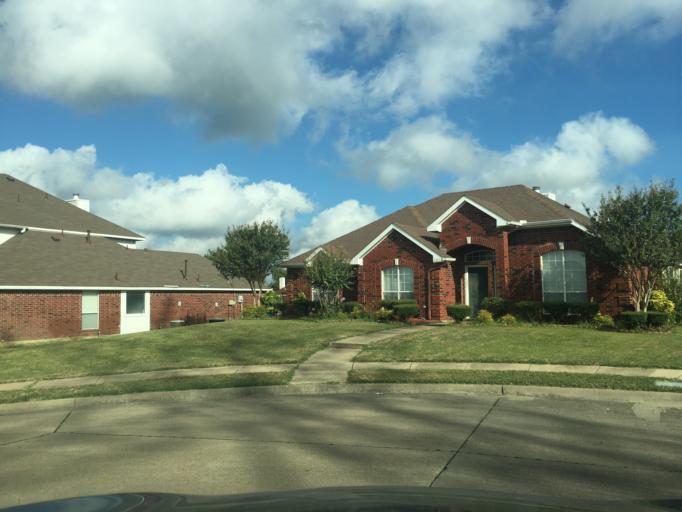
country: US
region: Texas
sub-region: Dallas County
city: Sachse
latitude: 32.9648
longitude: -96.5916
